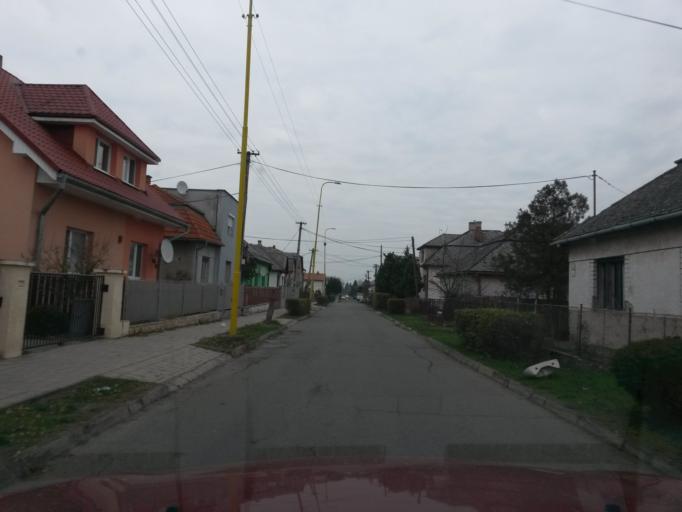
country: SK
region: Kosicky
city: Secovce
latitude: 48.6984
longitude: 21.6556
